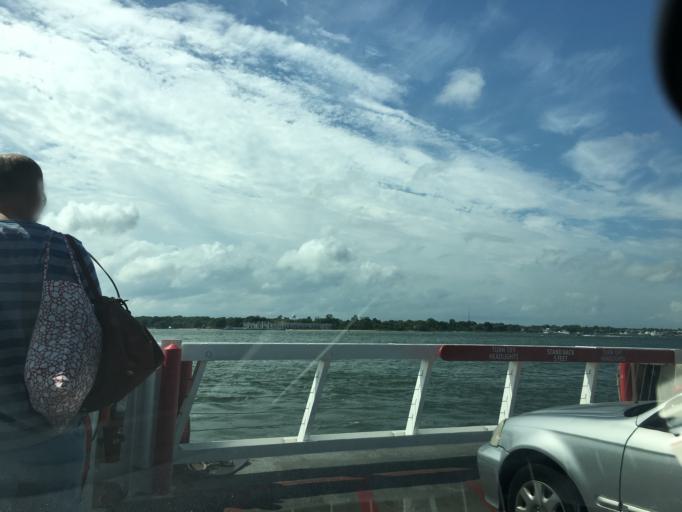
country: US
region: New York
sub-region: Suffolk County
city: Greenport
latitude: 41.1071
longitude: -72.3603
